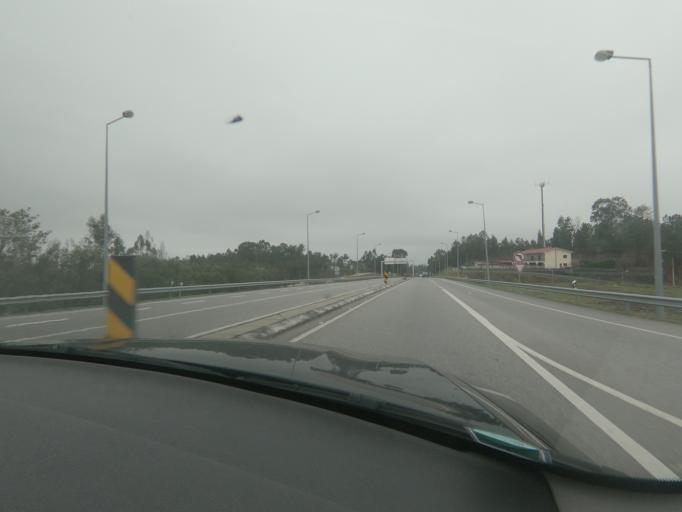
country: PT
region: Viseu
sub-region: Concelho de Tondela
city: Tondela
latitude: 40.5862
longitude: -8.0161
